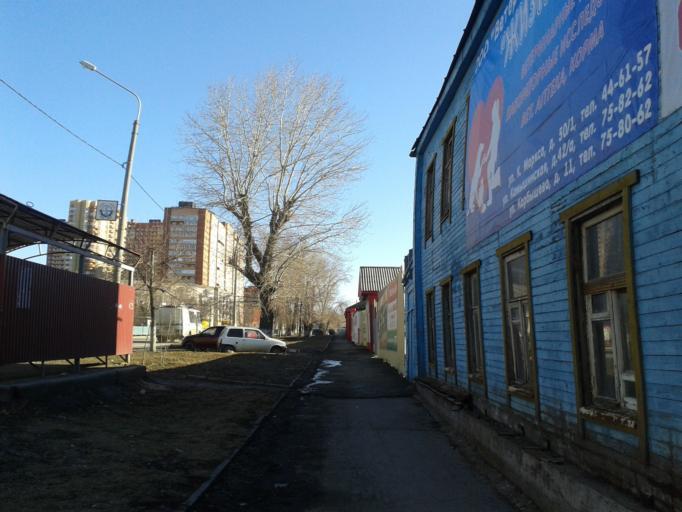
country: RU
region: Ulyanovsk
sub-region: Ulyanovskiy Rayon
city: Ulyanovsk
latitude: 54.2981
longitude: 48.3797
